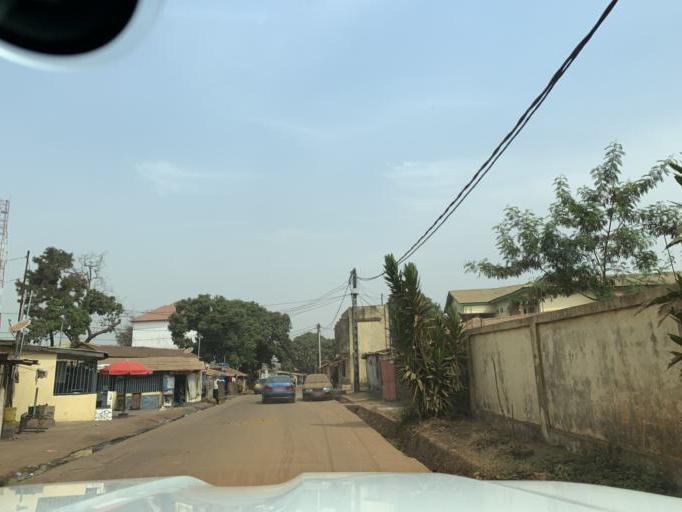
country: GN
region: Conakry
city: Conakry
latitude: 9.5520
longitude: -13.6689
